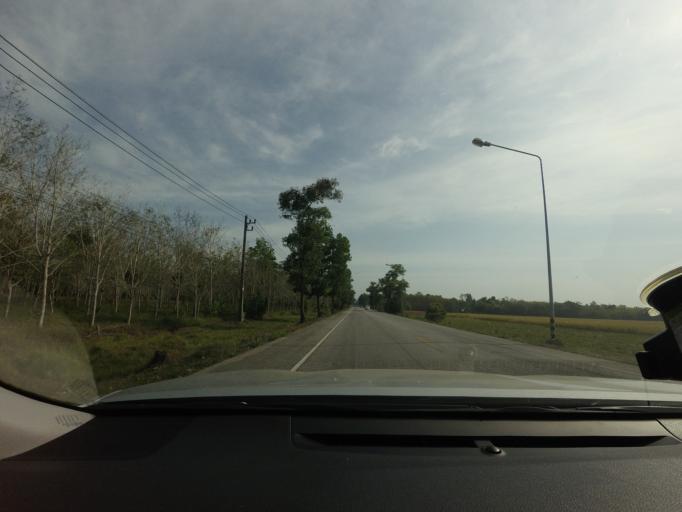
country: TH
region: Narathiwat
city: Ra-ngae
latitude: 6.3360
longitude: 101.7896
